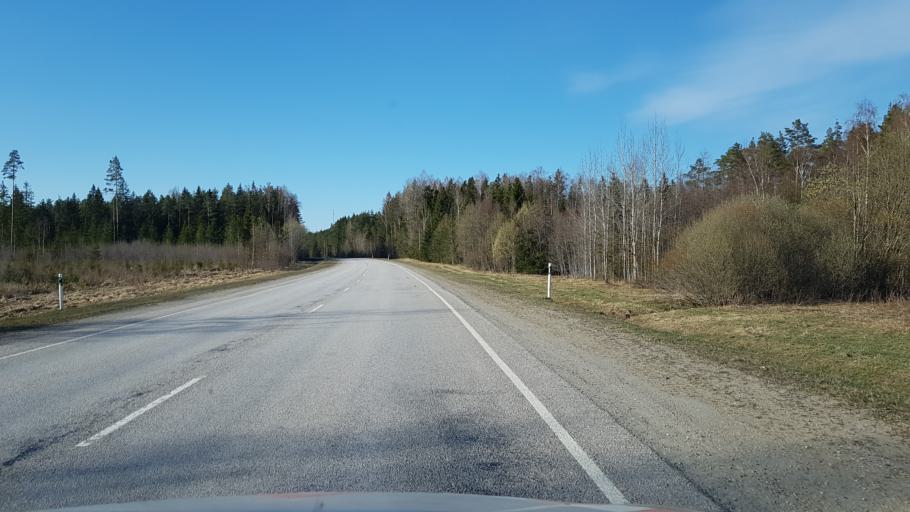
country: EE
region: Ida-Virumaa
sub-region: Johvi vald
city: Johvi
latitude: 59.1516
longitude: 27.3592
